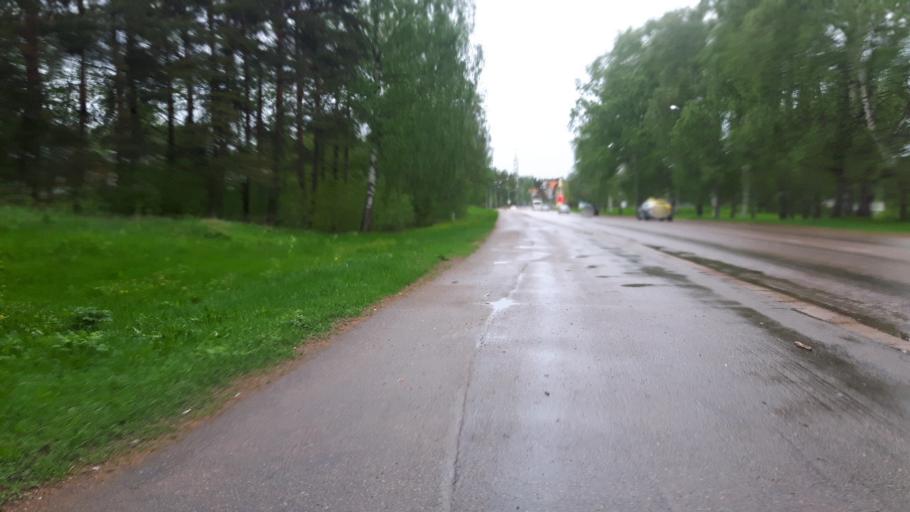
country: FI
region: Kymenlaakso
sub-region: Kotka-Hamina
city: Kotka
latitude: 60.4841
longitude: 26.9091
